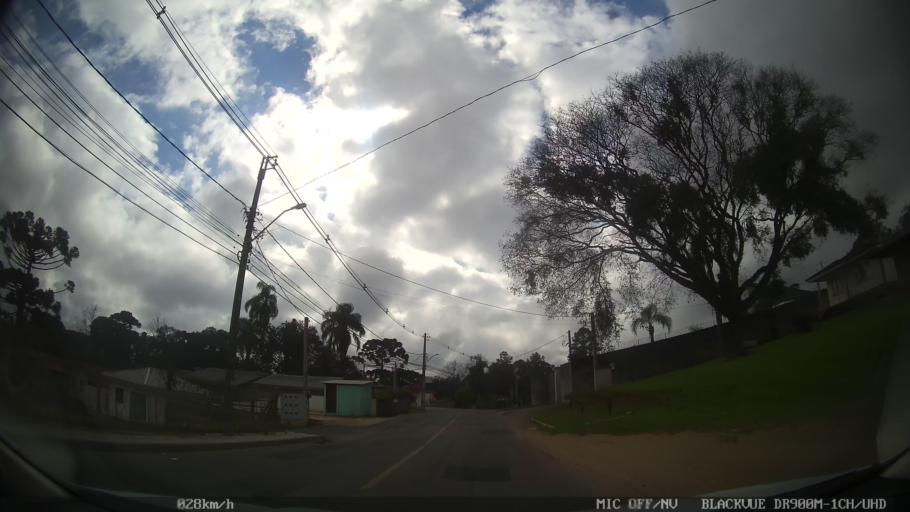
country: BR
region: Parana
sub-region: Colombo
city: Colombo
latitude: -25.3598
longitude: -49.2443
